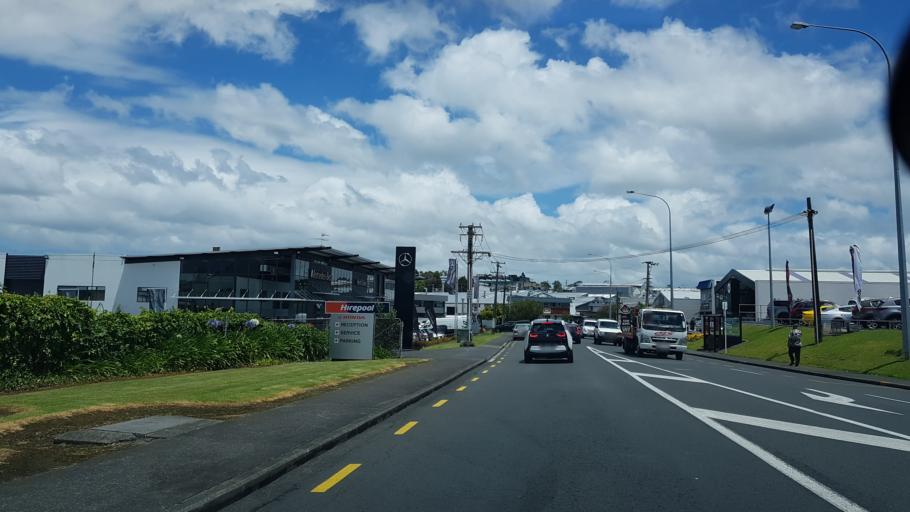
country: NZ
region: Auckland
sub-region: Auckland
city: North Shore
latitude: -36.7717
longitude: 174.7384
